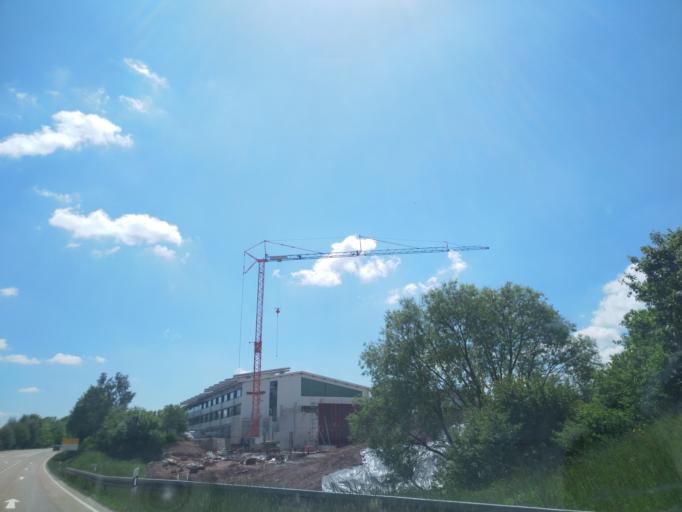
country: DE
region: Baden-Wuerttemberg
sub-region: Karlsruhe Region
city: Freudenstadt
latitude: 48.4685
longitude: 8.4354
